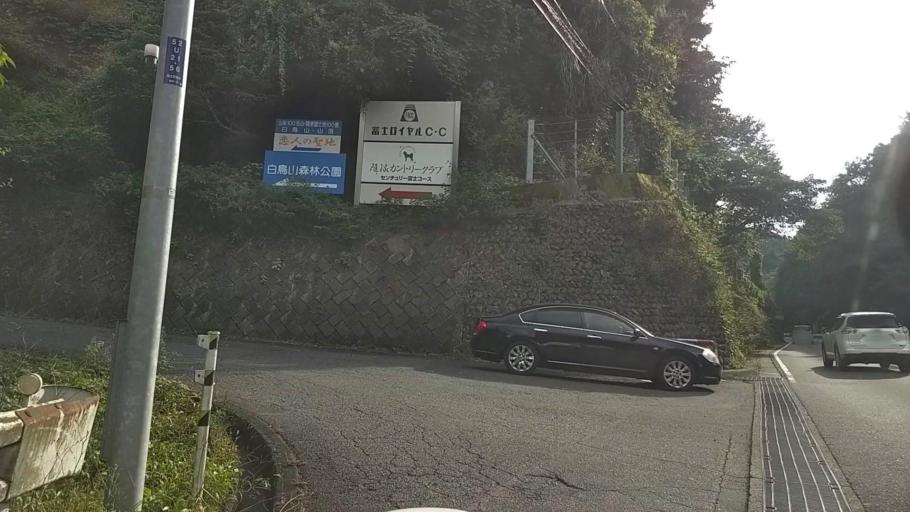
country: JP
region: Shizuoka
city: Fujinomiya
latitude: 35.2110
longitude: 138.5186
